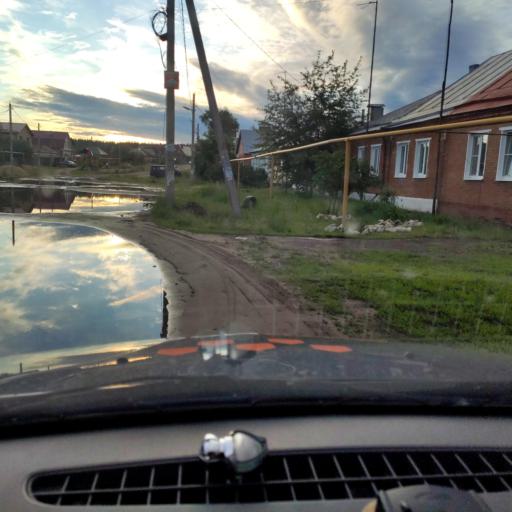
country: RU
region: Voronezj
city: Somovo
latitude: 51.7524
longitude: 39.3266
